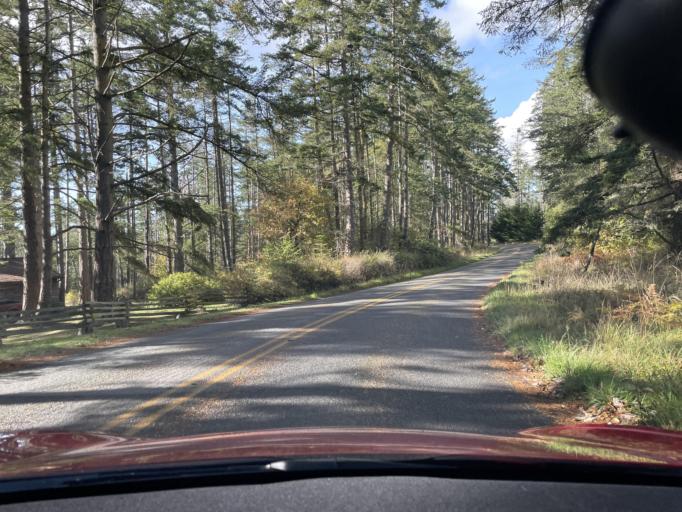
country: US
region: Washington
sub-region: San Juan County
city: Friday Harbor
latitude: 48.5048
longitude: -123.0189
